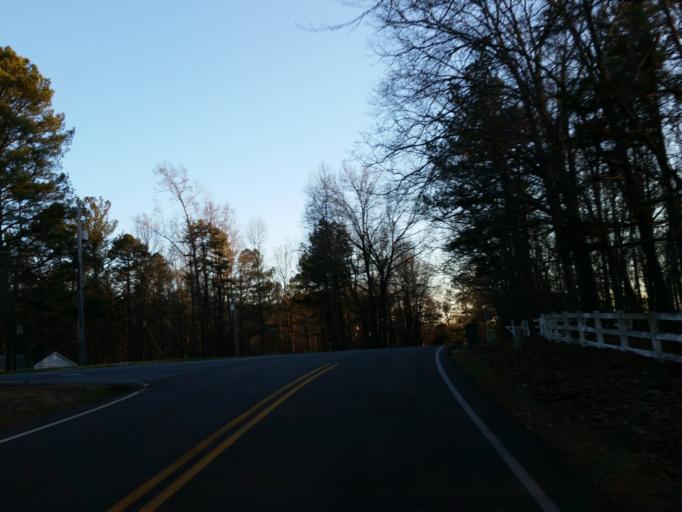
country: US
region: Georgia
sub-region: Cherokee County
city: Holly Springs
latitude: 34.1298
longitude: -84.4268
